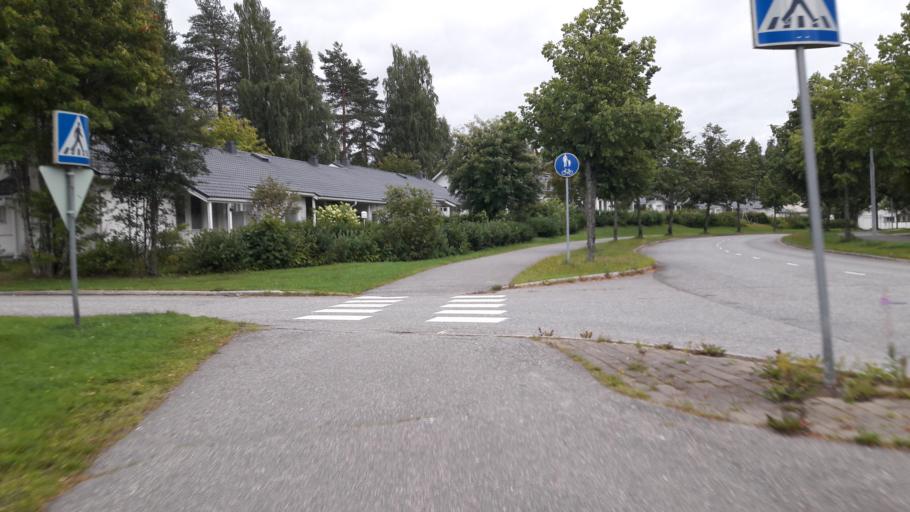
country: FI
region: North Karelia
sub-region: Joensuu
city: Joensuu
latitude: 62.6191
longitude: 29.6950
